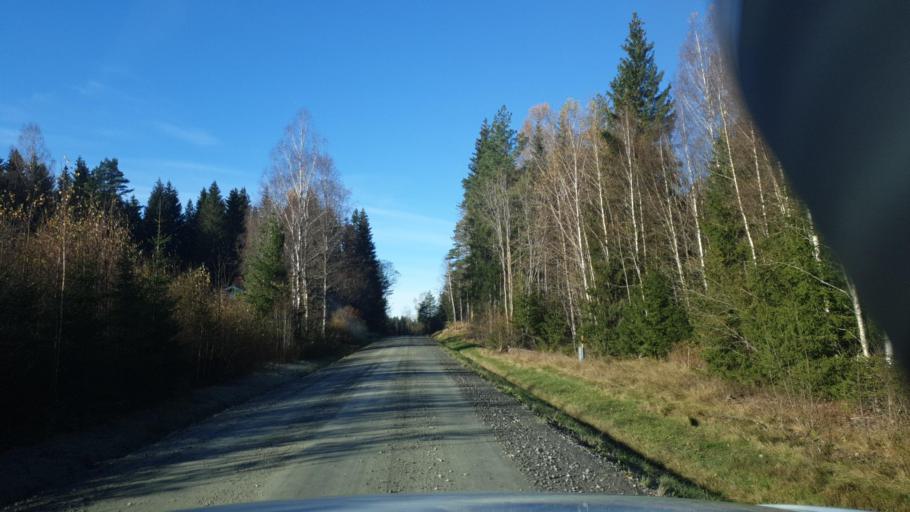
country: SE
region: Vaermland
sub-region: Karlstads Kommun
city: Edsvalla
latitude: 59.4507
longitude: 13.1340
